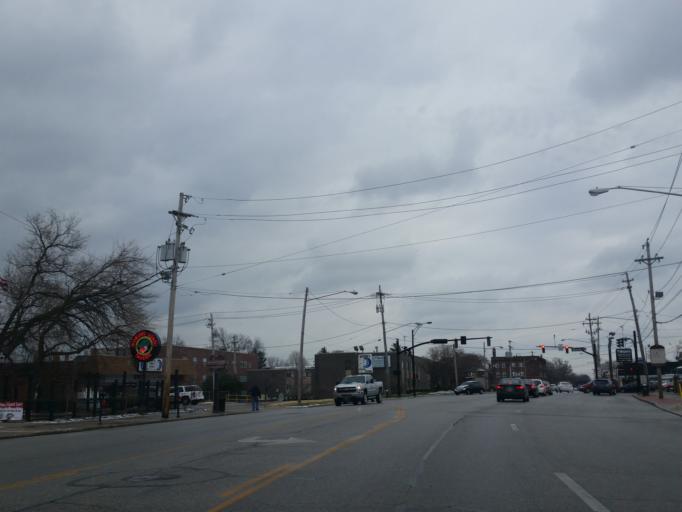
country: US
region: Ohio
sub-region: Cuyahoga County
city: Lakewood
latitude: 41.4855
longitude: -81.7907
